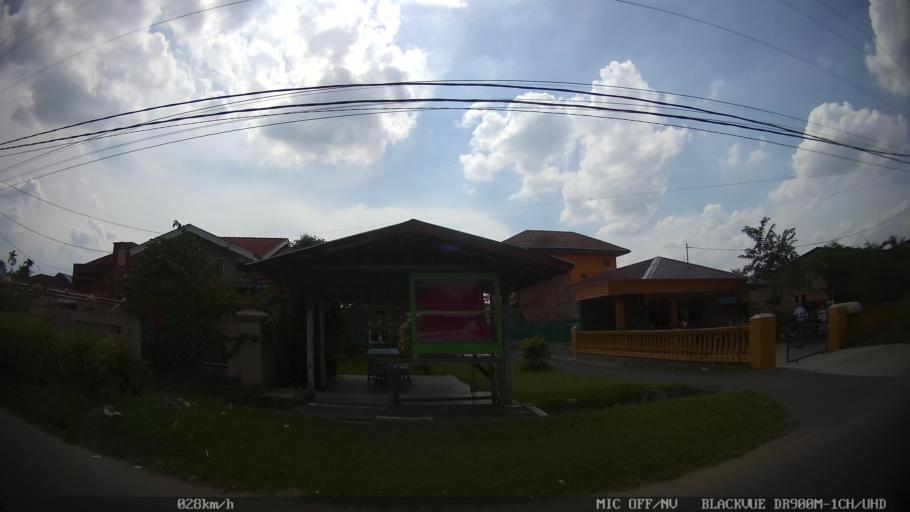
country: ID
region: North Sumatra
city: Binjai
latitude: 3.6256
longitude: 98.5012
